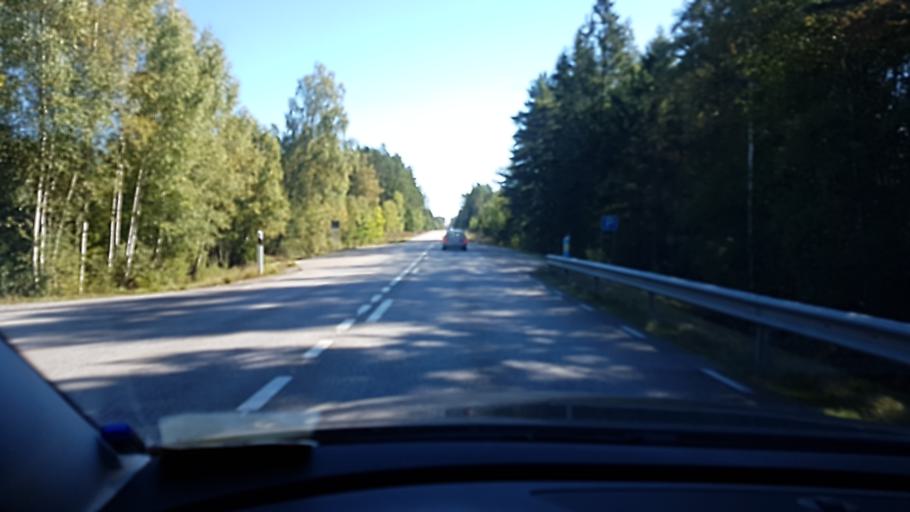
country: SE
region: Kronoberg
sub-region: Lessebo Kommun
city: Lessebo
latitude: 56.7299
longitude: 15.3140
